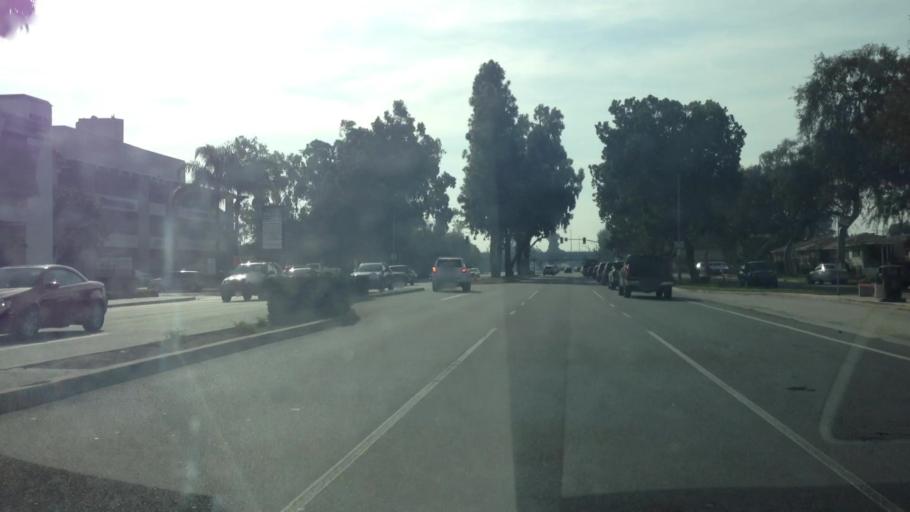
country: US
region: California
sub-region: Los Angeles County
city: Signal Hill
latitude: 33.8067
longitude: -118.1253
